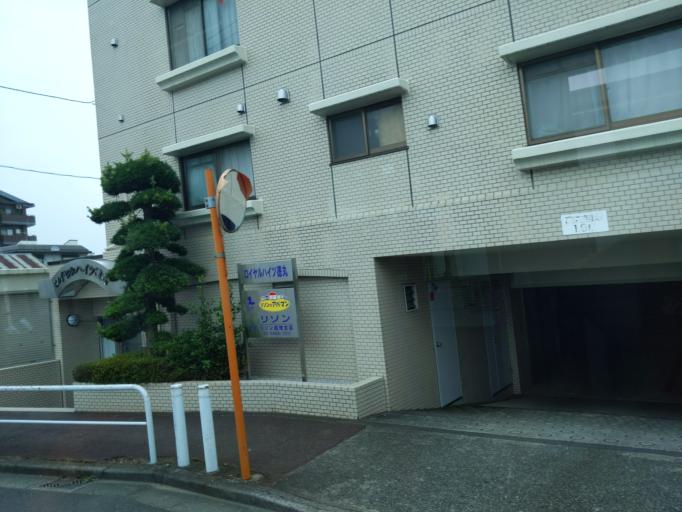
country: JP
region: Saitama
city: Wako
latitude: 35.7737
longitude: 139.6556
